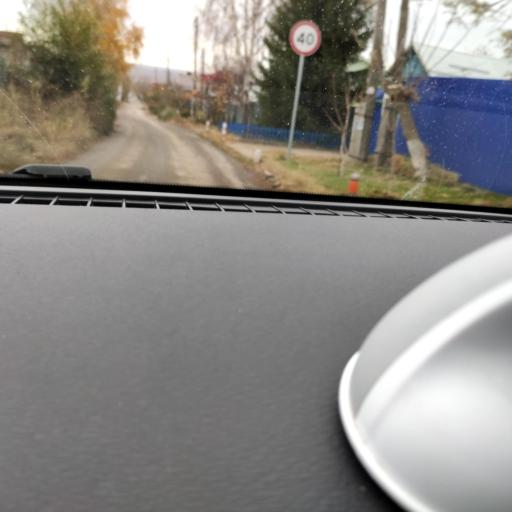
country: RU
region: Samara
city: Samara
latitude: 53.1824
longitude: 50.1874
